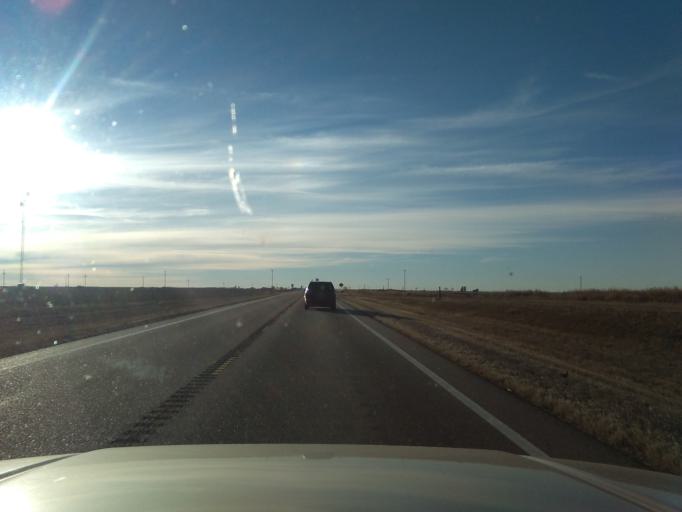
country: US
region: Kansas
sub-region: Thomas County
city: Colby
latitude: 39.4556
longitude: -100.7912
